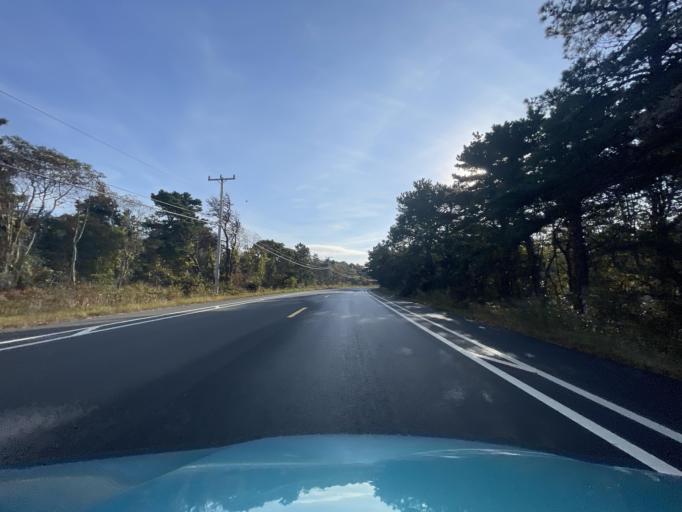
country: US
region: Massachusetts
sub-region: Bristol County
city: Head of Westport
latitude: 41.5074
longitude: -71.0478
